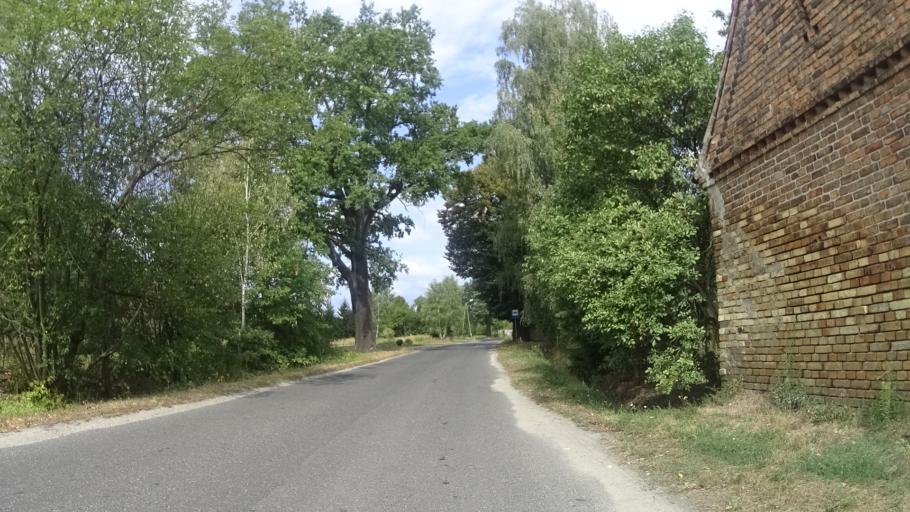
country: PL
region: Lubusz
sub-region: Powiat zarski
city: Leknica
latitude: 51.5388
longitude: 14.8020
